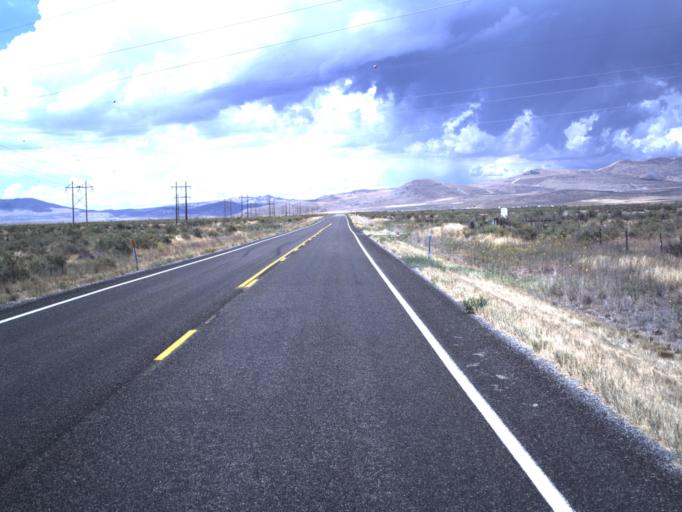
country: US
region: Utah
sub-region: Box Elder County
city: Tremonton
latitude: 41.5965
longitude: -112.2909
